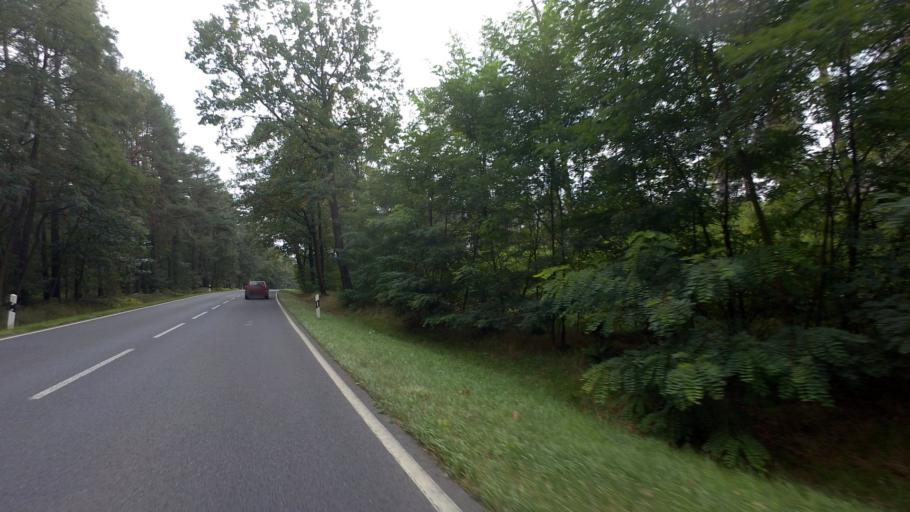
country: DE
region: Brandenburg
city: Sonnewalde
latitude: 51.7391
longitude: 13.6816
